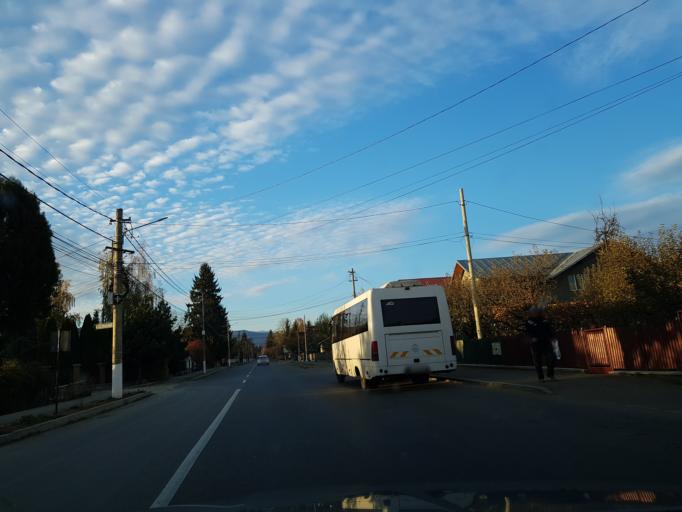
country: RO
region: Prahova
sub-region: Oras Breaza
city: Breaza
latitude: 45.1889
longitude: 25.6606
